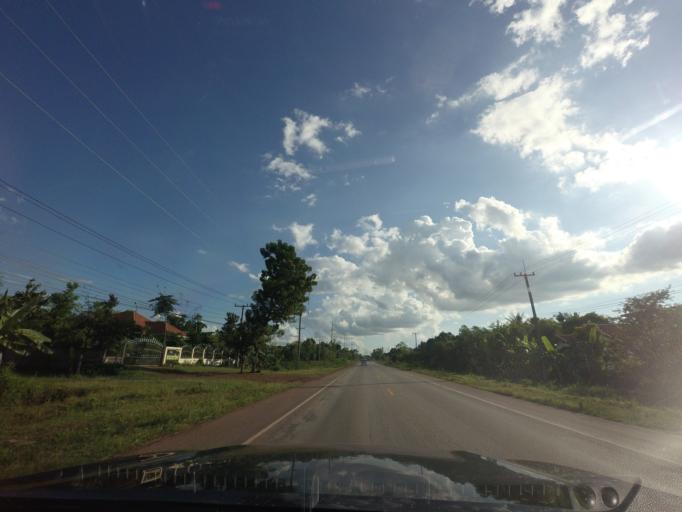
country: TH
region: Changwat Udon Thani
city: Thung Fon
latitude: 17.4941
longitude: 103.2002
